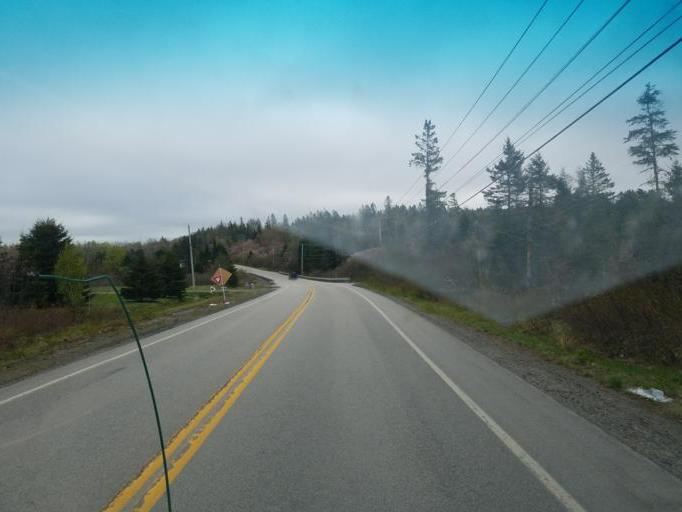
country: US
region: Maine
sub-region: Washington County
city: Eastport
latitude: 44.7907
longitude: -67.1612
